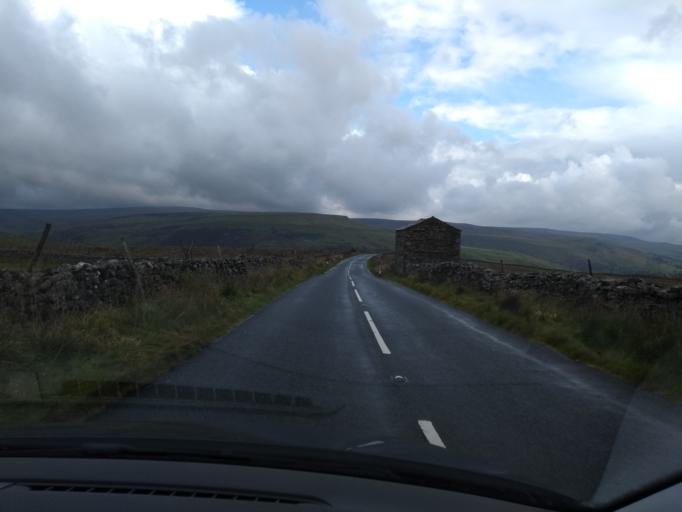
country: GB
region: England
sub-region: Cumbria
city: Kirkby Stephen
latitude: 54.3726
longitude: -2.1830
